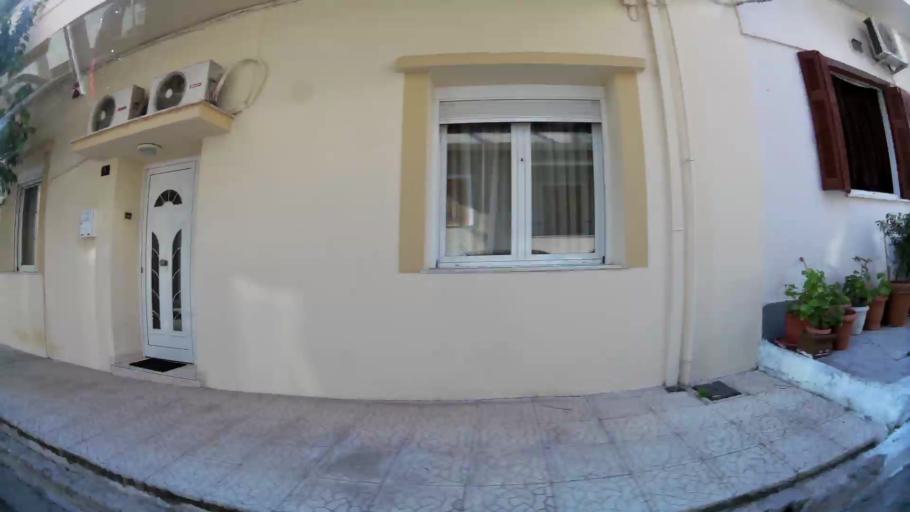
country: GR
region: Attica
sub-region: Nomos Piraios
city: Keratsini
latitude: 37.9656
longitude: 23.6266
